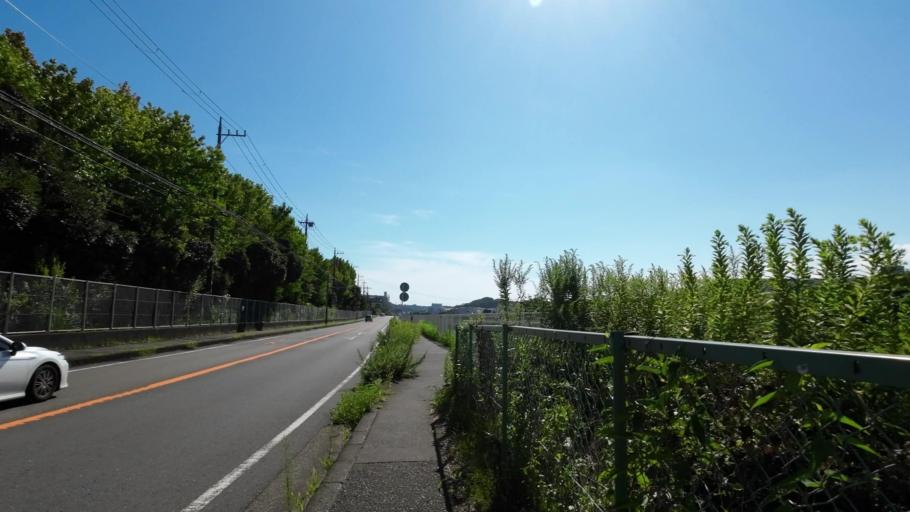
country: JP
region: Kanagawa
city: Fujisawa
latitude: 35.3458
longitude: 139.5160
